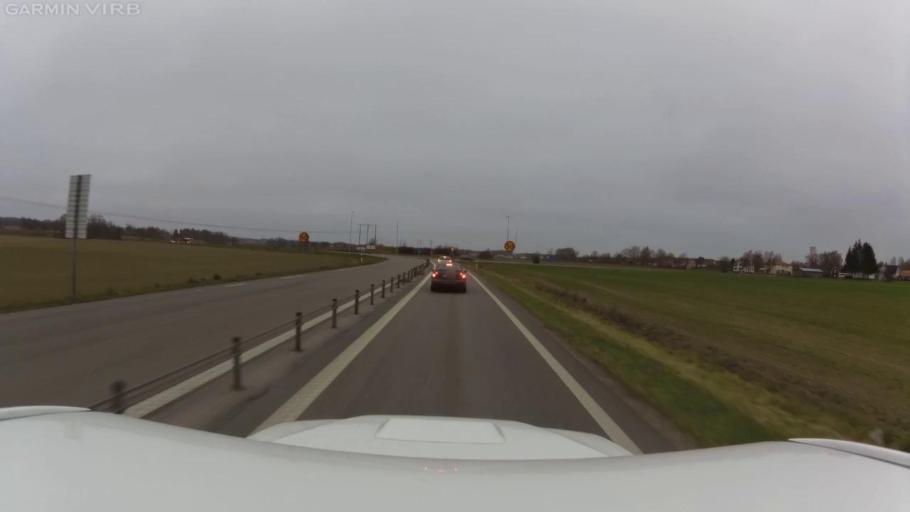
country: SE
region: OEstergoetland
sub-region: Linkopings Kommun
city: Vikingstad
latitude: 58.3765
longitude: 15.4395
